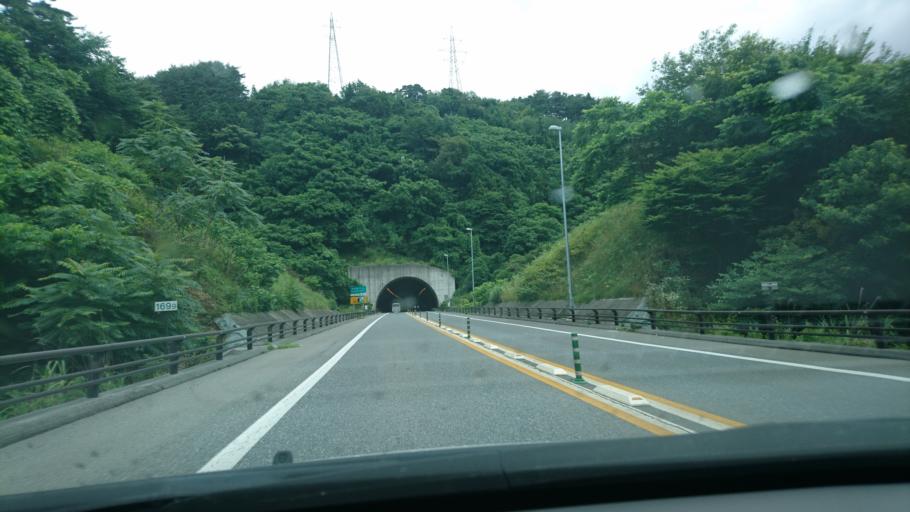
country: JP
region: Iwate
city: Ofunato
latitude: 39.0853
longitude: 141.7003
